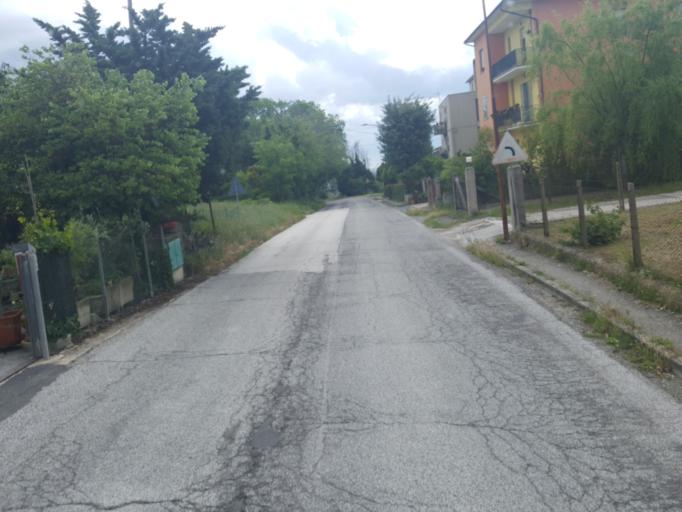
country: IT
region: The Marches
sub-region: Provincia di Macerata
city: Pollenza
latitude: 43.2590
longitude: 13.3592
